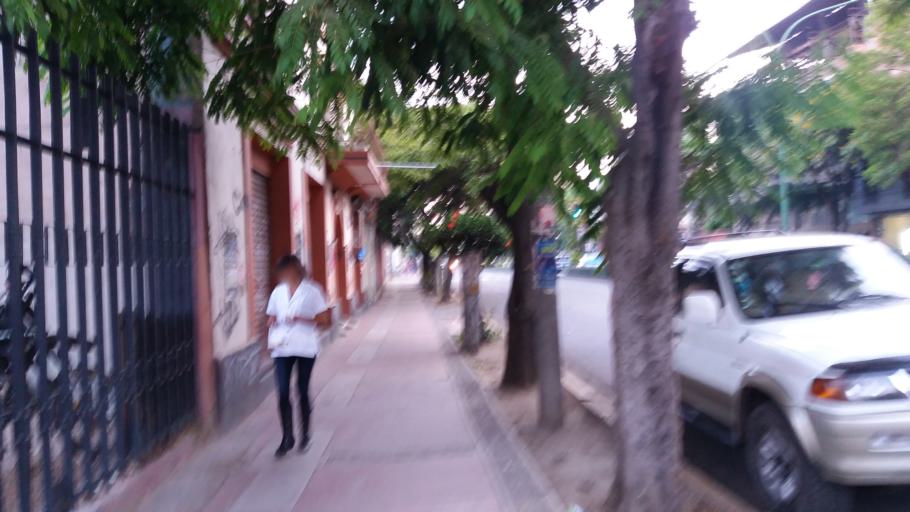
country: BO
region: Cochabamba
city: Cochabamba
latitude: -17.3887
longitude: -66.1596
